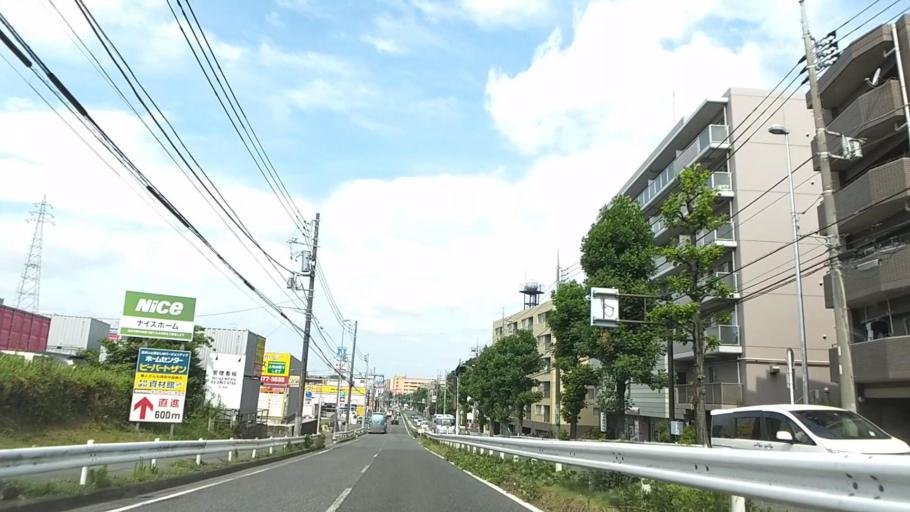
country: JP
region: Kanagawa
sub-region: Kawasaki-shi
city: Kawasaki
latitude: 35.5248
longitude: 139.6570
